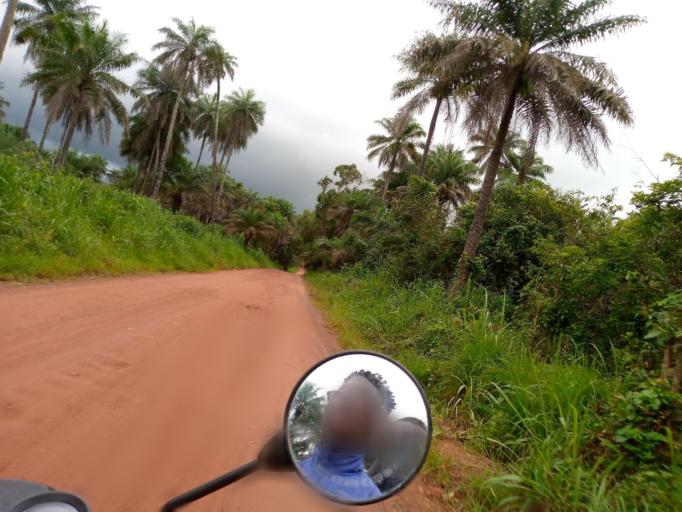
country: SL
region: Northern Province
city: Port Loko
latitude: 8.8727
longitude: -12.7272
